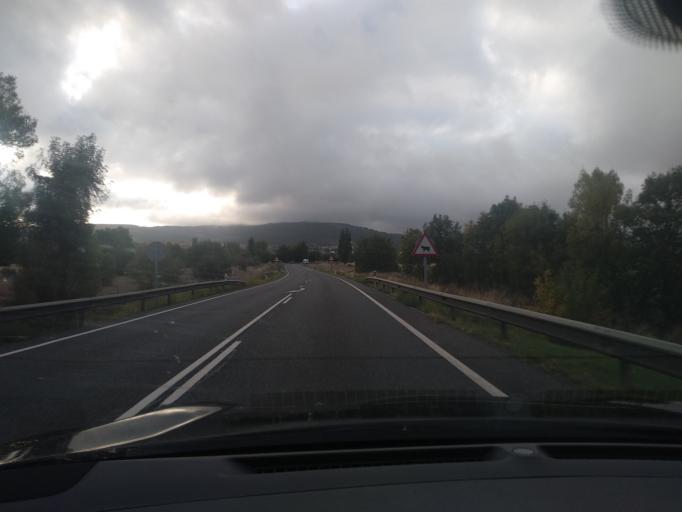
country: ES
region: Castille and Leon
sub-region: Provincia de Segovia
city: Otero de Herreros
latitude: 40.7528
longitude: -4.2029
